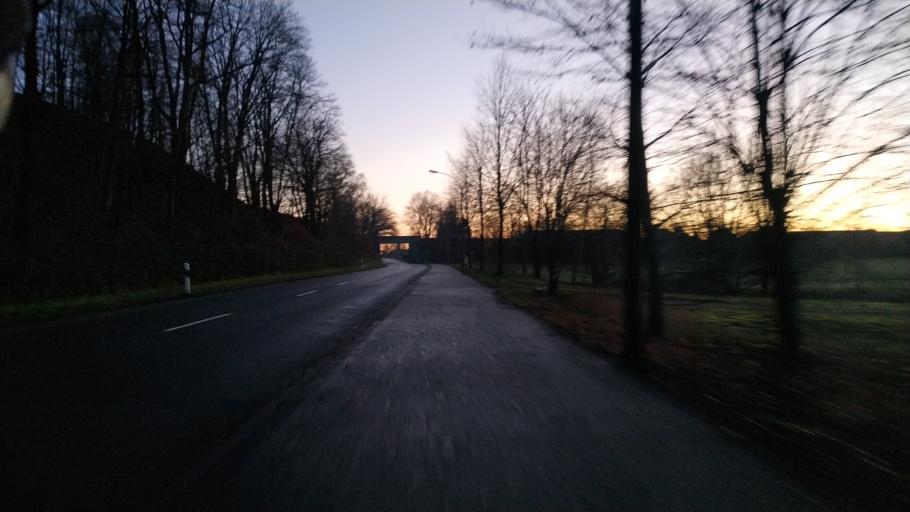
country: DE
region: North Rhine-Westphalia
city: Ibbenburen
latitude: 52.2902
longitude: 7.7336
